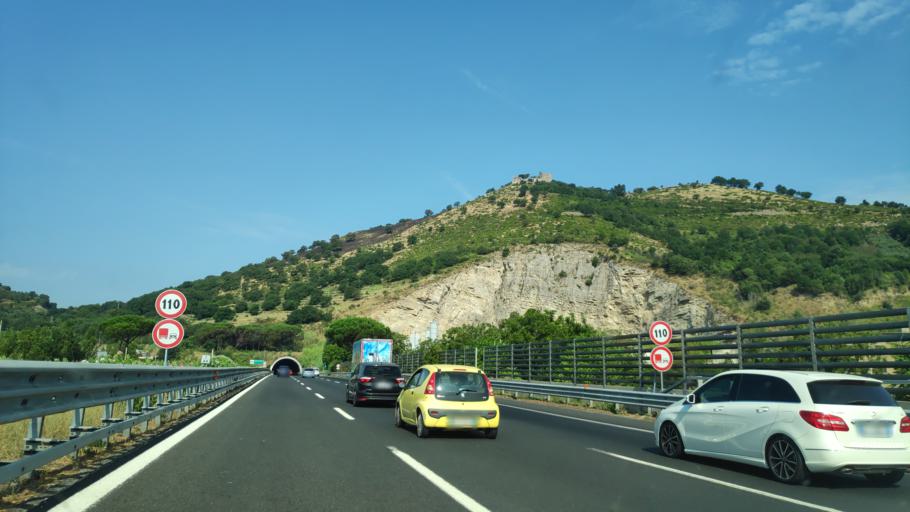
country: IT
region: Campania
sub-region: Provincia di Salerno
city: Lanzara
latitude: 40.7718
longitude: 14.6643
